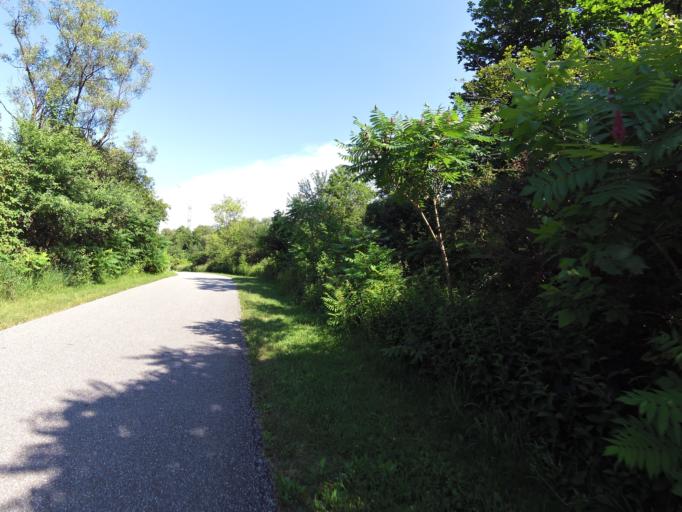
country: CA
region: Ontario
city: Etobicoke
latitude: 43.7277
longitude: -79.5587
